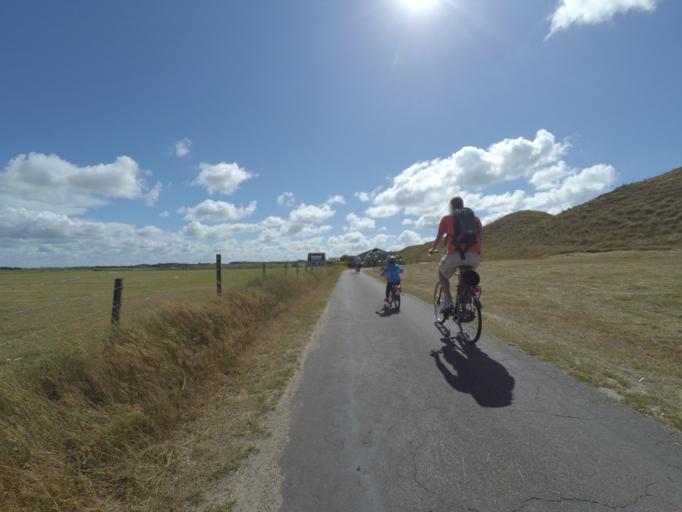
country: NL
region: North Holland
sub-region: Gemeente Texel
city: Den Burg
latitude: 53.1170
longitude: 4.8007
